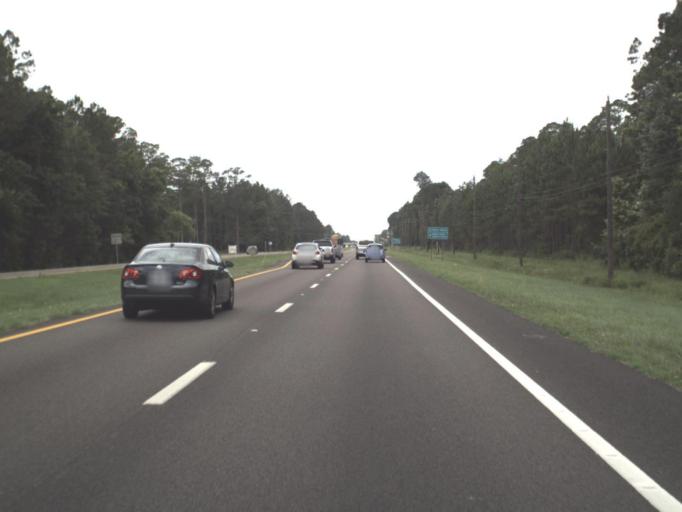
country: US
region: Florida
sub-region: Nassau County
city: Yulee
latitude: 30.6241
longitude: -81.6336
